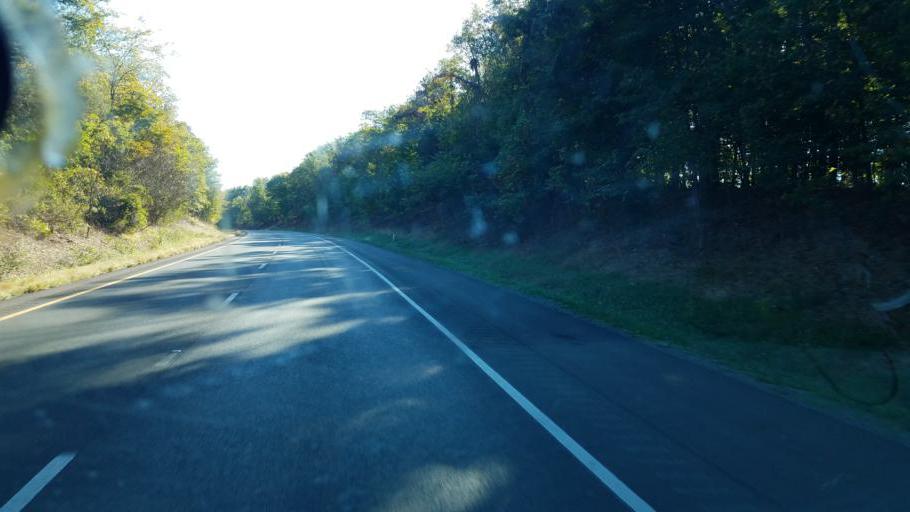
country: US
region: West Virginia
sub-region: Berkeley County
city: Martinsburg
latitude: 39.6234
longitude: -78.0056
